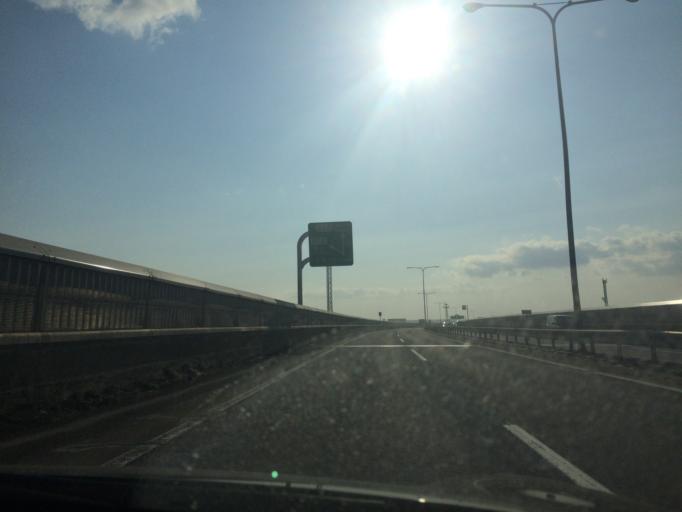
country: JP
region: Hokkaido
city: Sapporo
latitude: 43.0902
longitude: 141.4111
